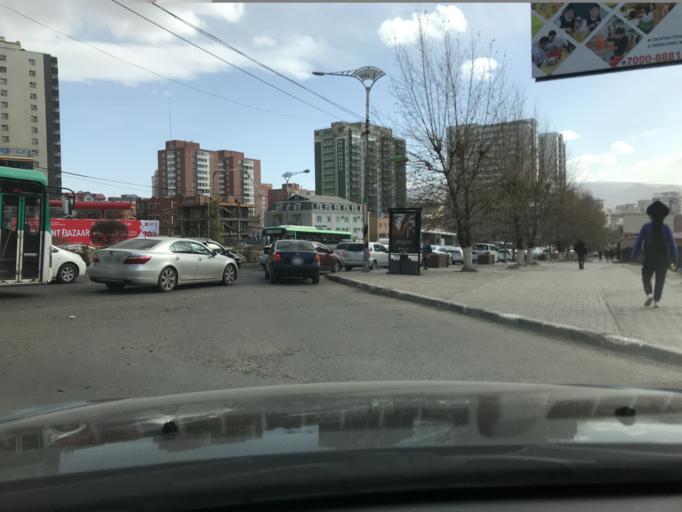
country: MN
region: Ulaanbaatar
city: Ulaanbaatar
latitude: 47.9184
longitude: 106.9430
